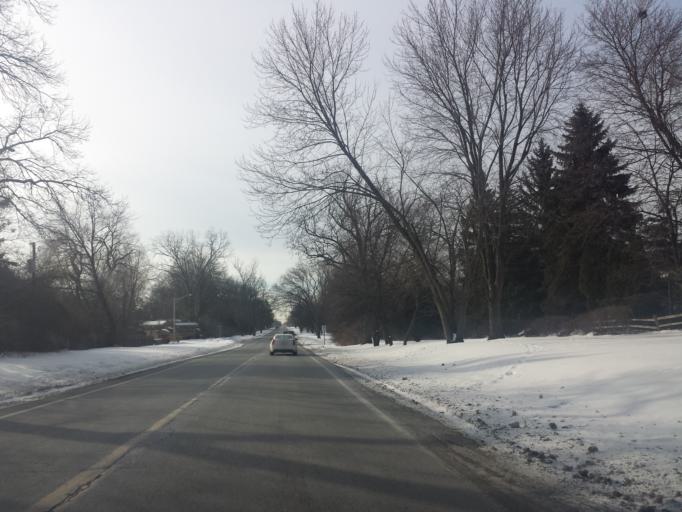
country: US
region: Michigan
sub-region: Oakland County
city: Franklin
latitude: 42.5395
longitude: -83.3409
